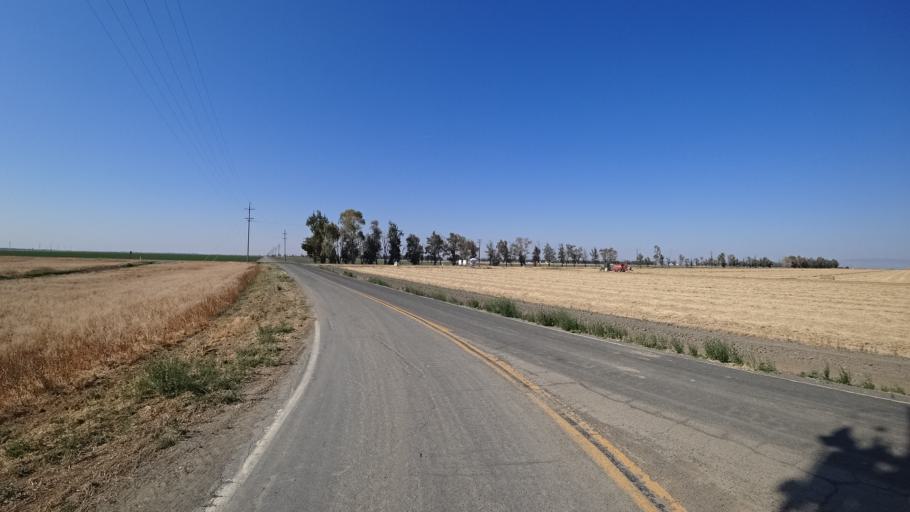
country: US
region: California
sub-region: Kings County
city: Lemoore Station
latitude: 36.3439
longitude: -119.9053
